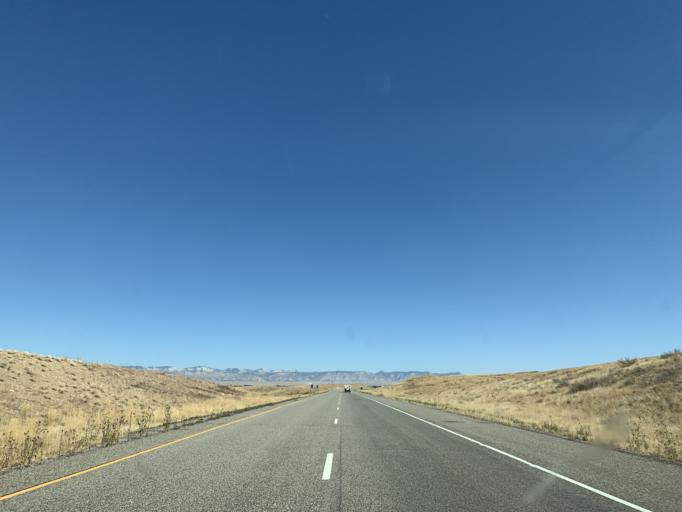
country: US
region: Colorado
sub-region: Mesa County
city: Loma
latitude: 39.2283
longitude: -108.9184
